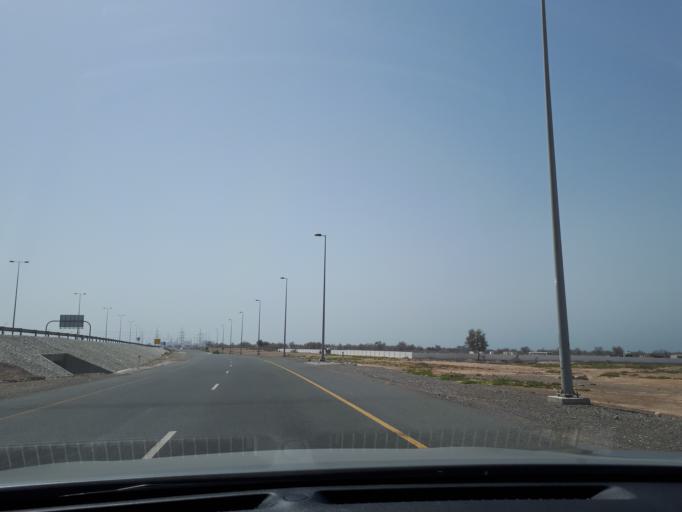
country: OM
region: Al Batinah
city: Barka'
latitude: 23.6976
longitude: 58.0177
